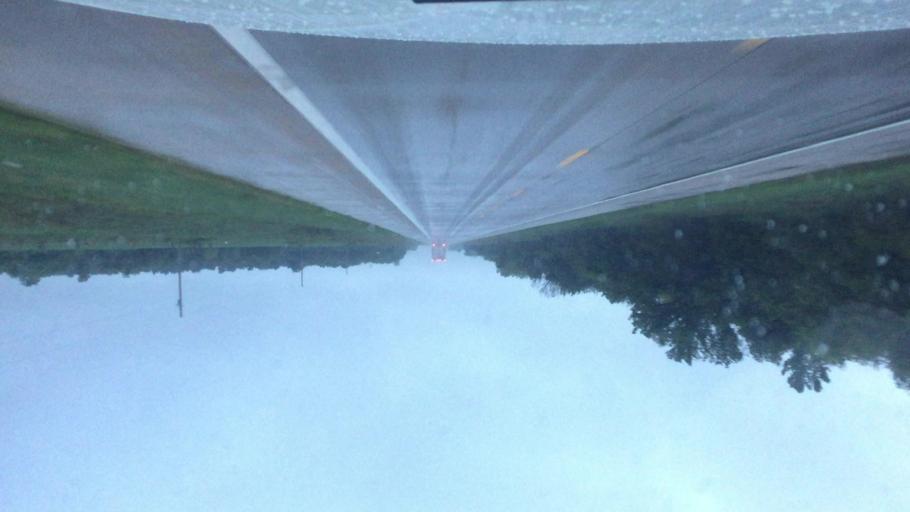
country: US
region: Kansas
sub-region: Neosho County
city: Chanute
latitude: 37.5519
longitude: -95.4709
